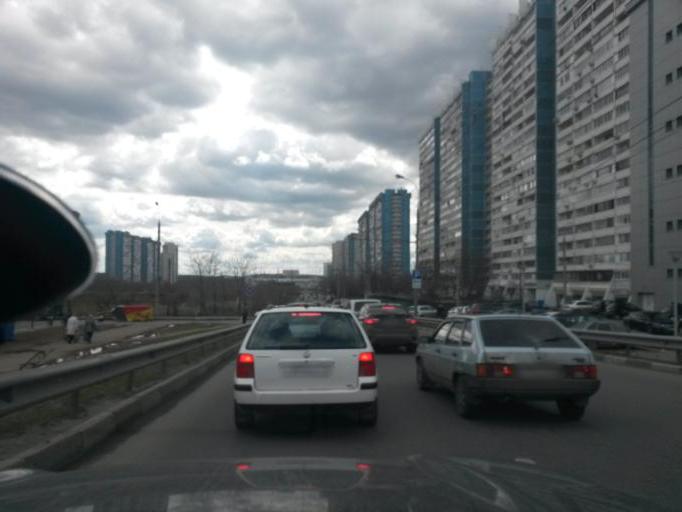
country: RU
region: Moscow
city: Yasenevo
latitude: 55.6059
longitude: 37.5323
